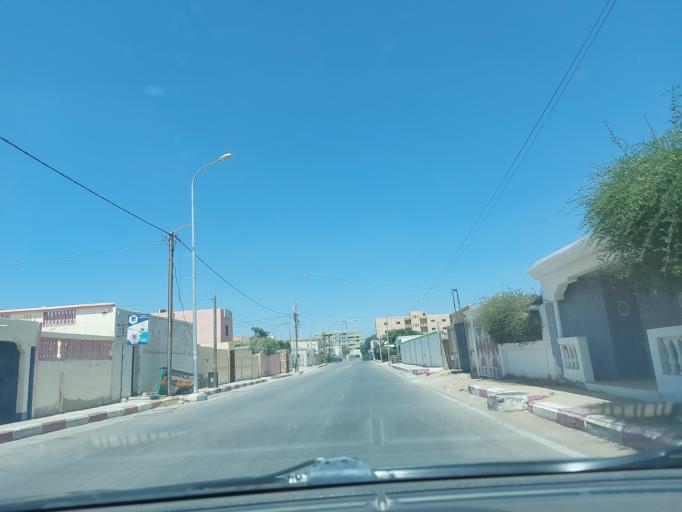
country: MR
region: Nouakchott
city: Nouakchott
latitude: 18.0924
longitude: -15.9747
